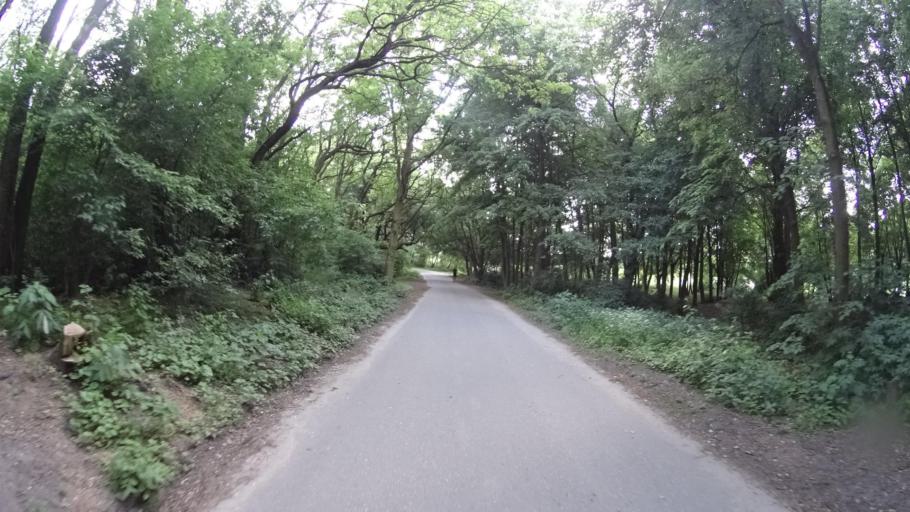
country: PL
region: Masovian Voivodeship
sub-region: Warszawa
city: Kabaty
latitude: 52.1163
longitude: 21.0852
